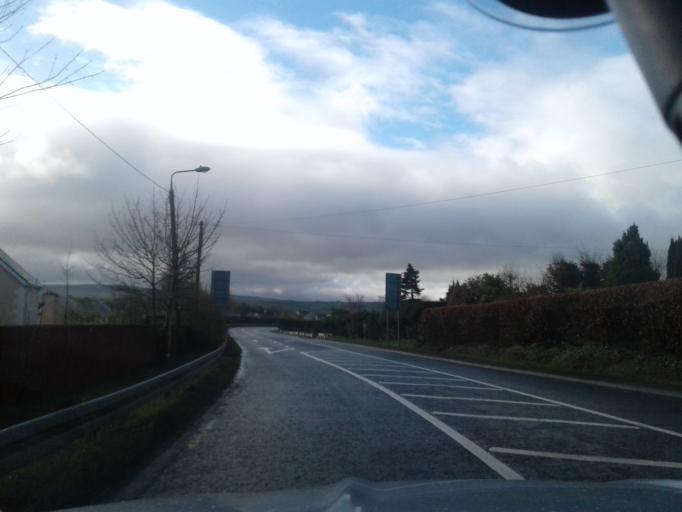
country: IE
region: Ulster
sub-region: County Donegal
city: Letterkenny
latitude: 54.9644
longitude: -7.6922
